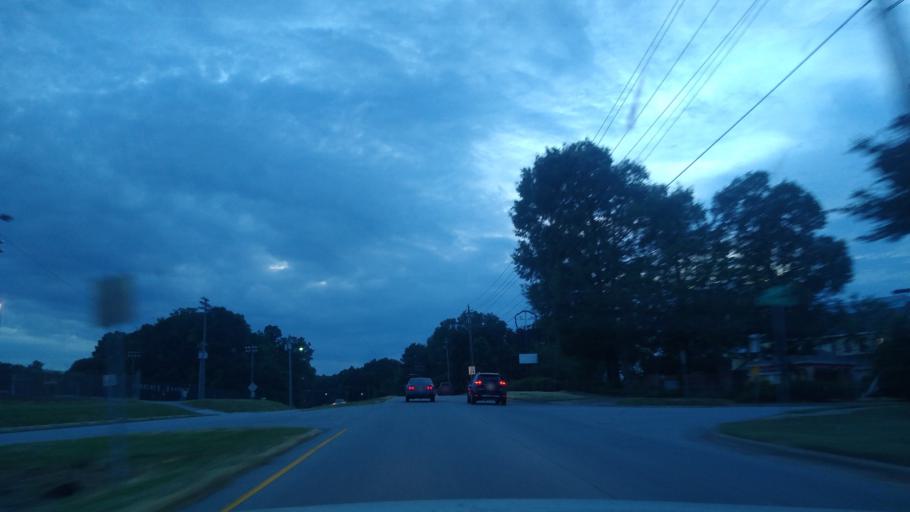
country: US
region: North Carolina
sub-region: Guilford County
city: Greensboro
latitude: 36.1111
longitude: -79.7834
